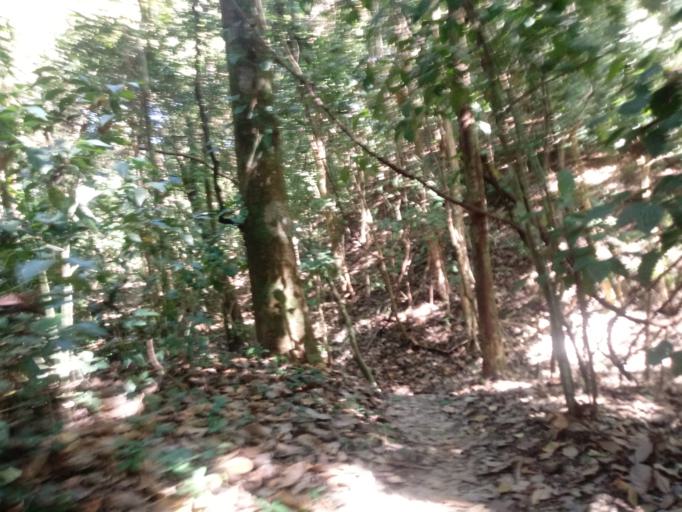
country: CR
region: Puntarenas
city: Paquera
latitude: 9.5832
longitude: -85.0993
